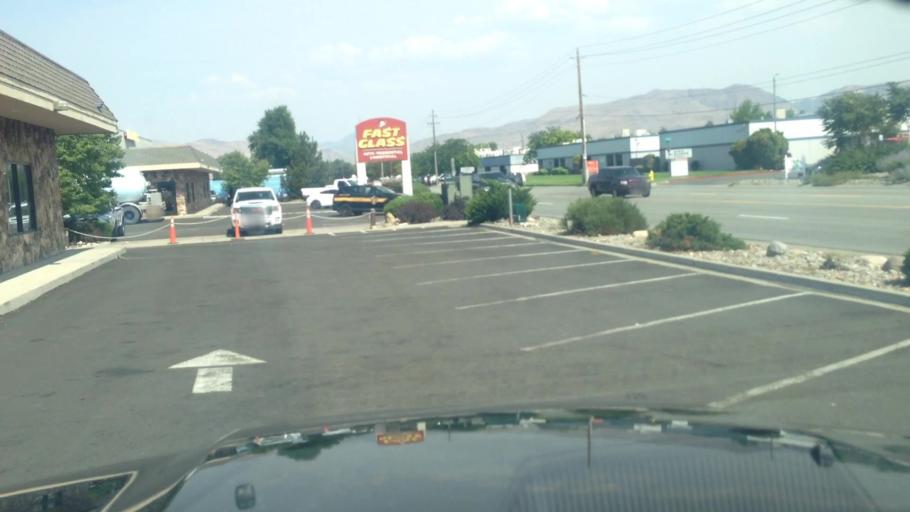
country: US
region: Nevada
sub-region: Washoe County
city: Sparks
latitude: 39.5236
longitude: -119.7653
